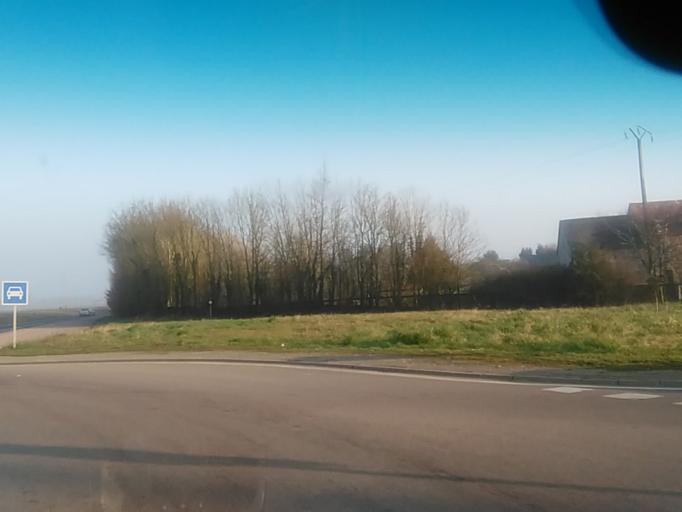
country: FR
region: Lower Normandy
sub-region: Departement du Calvados
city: Falaise
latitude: 48.8867
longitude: -0.2186
